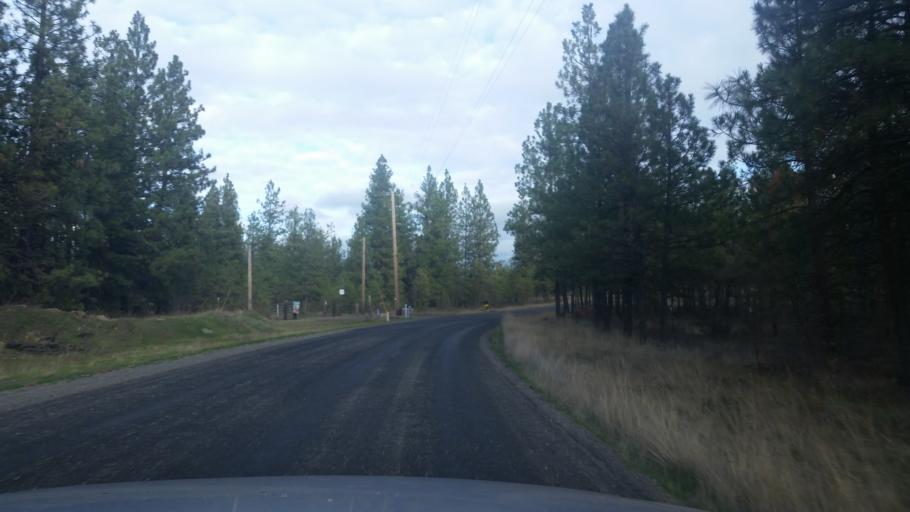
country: US
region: Washington
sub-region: Spokane County
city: Cheney
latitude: 47.4341
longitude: -117.4643
